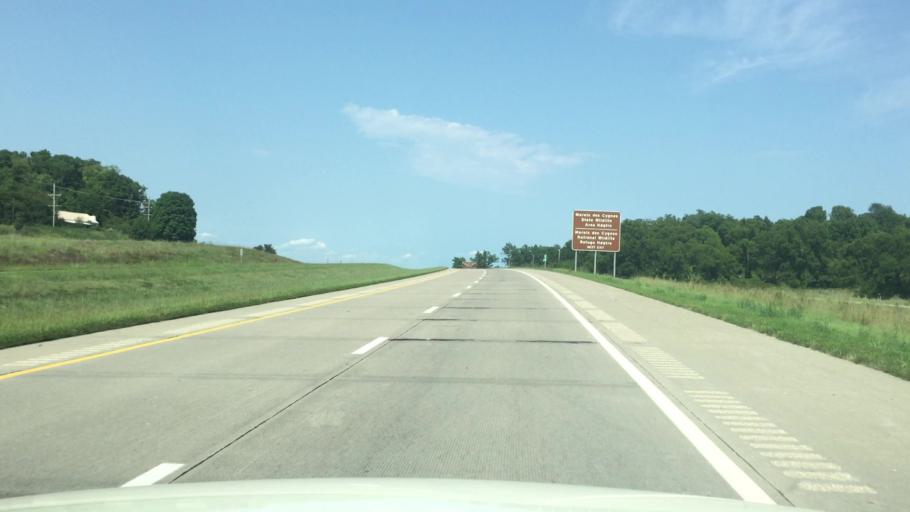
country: US
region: Kansas
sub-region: Linn County
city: Pleasanton
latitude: 38.2544
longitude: -94.6793
